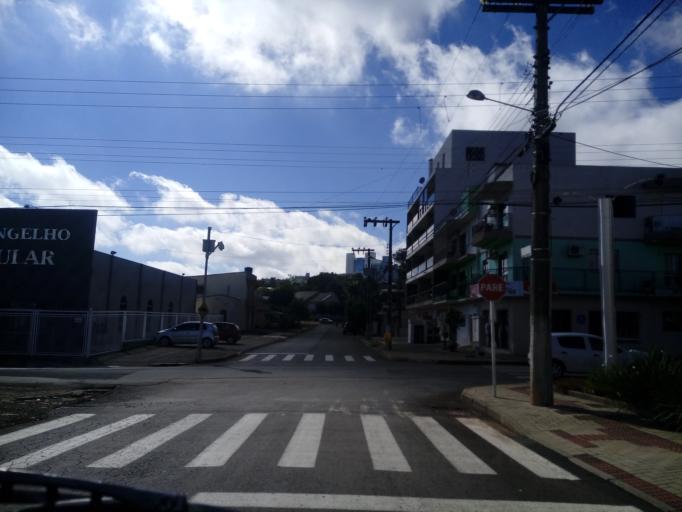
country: BR
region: Santa Catarina
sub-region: Chapeco
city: Chapeco
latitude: -27.1119
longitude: -52.6039
